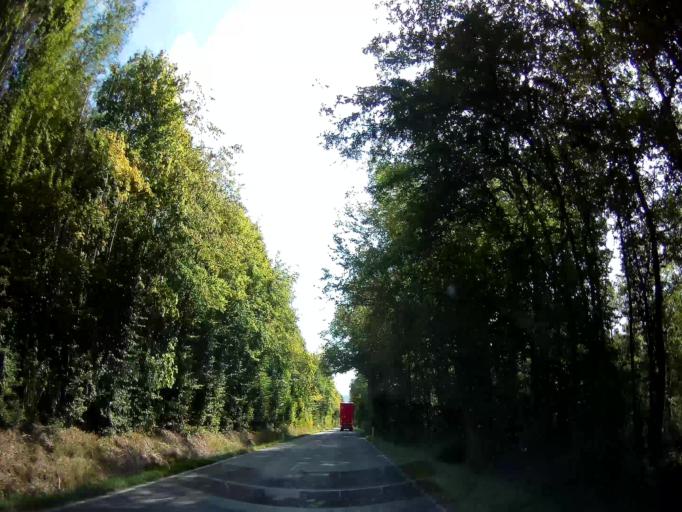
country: BE
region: Wallonia
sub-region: Province de Namur
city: Rochefort
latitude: 50.1675
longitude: 5.1691
